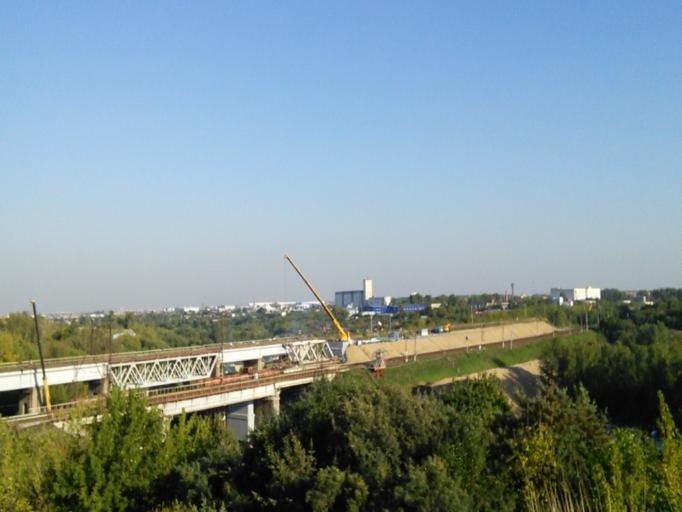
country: RU
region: Moskovskaya
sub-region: Podol'skiy Rayon
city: Podol'sk
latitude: 55.4505
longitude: 37.5636
